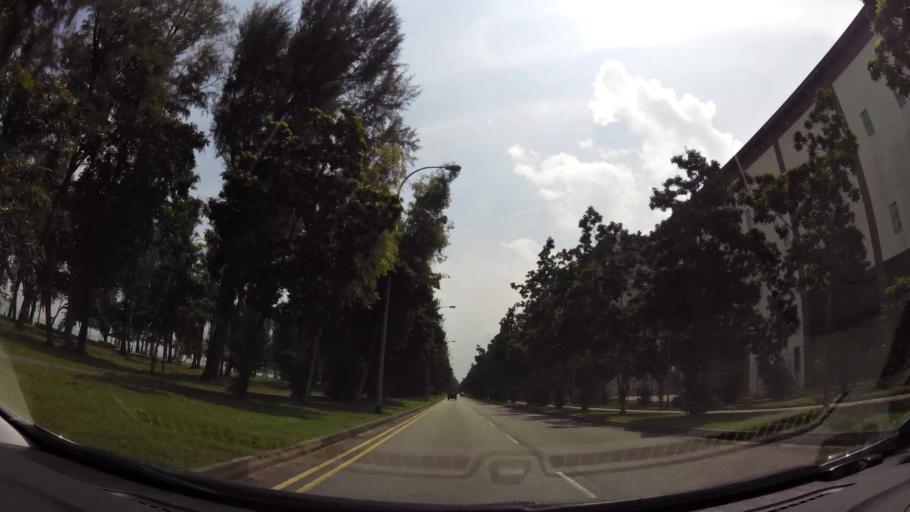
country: MY
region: Johor
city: Kampung Pasir Gudang Baru
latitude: 1.3816
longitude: 104.0017
